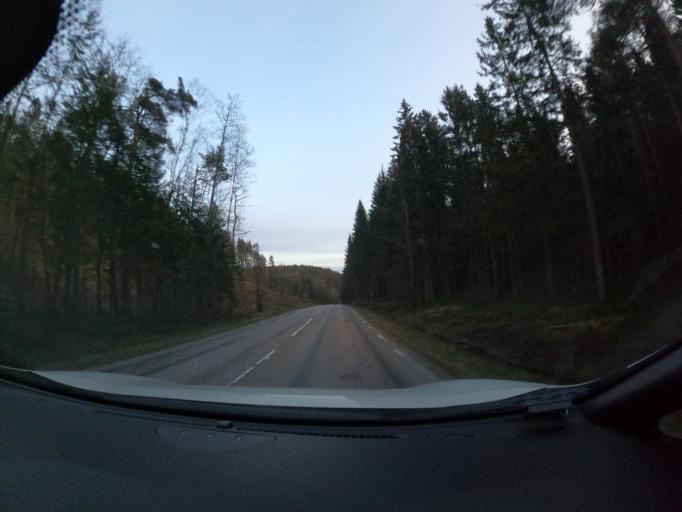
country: SE
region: Vaestra Goetaland
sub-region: Harryda Kommun
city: Landvetter
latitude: 57.6275
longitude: 12.1809
